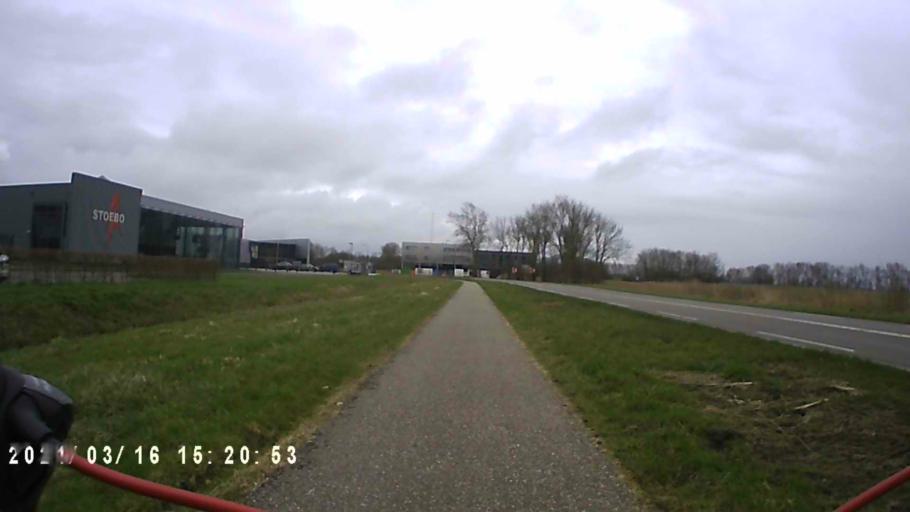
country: NL
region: Friesland
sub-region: Sudwest Fryslan
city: Bolsward
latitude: 53.0643
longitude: 5.5023
